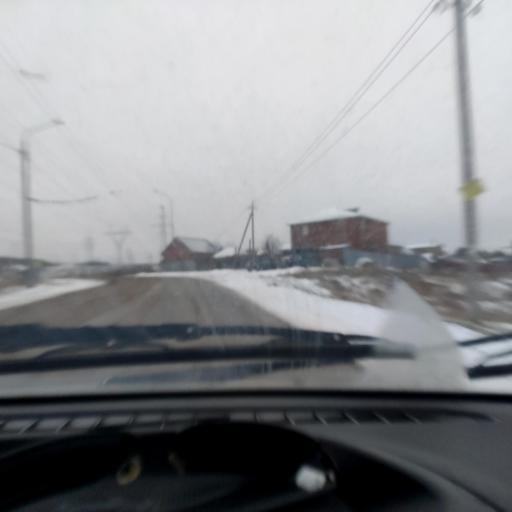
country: RU
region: Samara
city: Zhigulevsk
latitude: 53.4897
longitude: 49.5279
